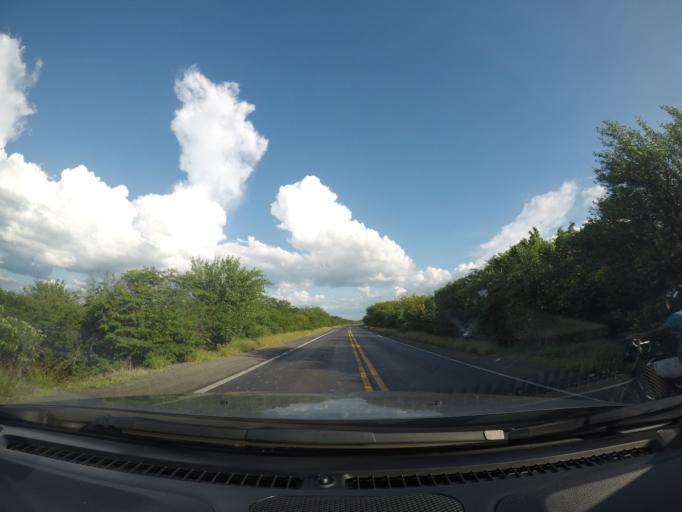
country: BR
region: Bahia
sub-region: Oliveira Dos Brejinhos
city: Oliveira dos Brejinhos
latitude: -12.0911
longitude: -42.9297
